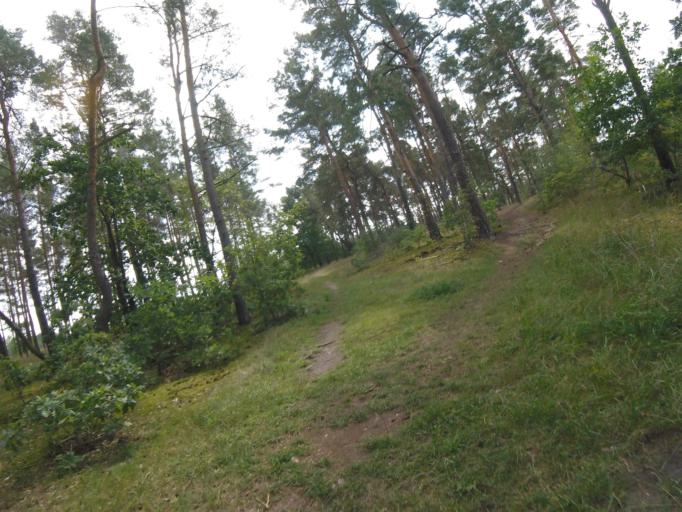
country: DE
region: Brandenburg
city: Bestensee
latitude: 52.2835
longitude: 13.6708
